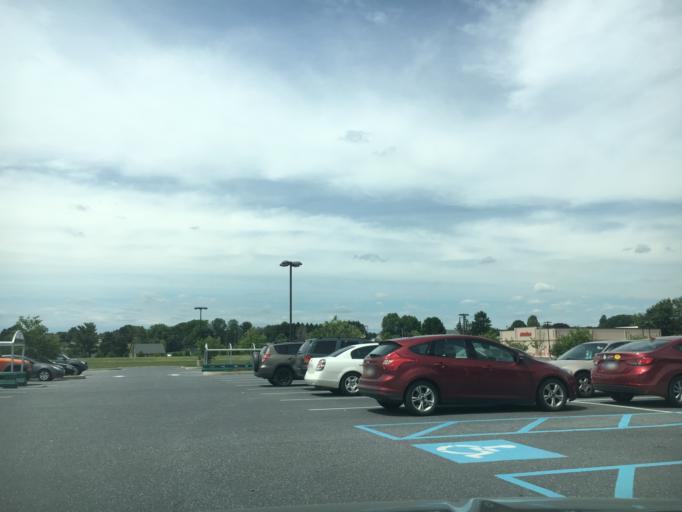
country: US
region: Pennsylvania
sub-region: Berks County
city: Kutztown
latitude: 40.5032
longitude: -75.7893
